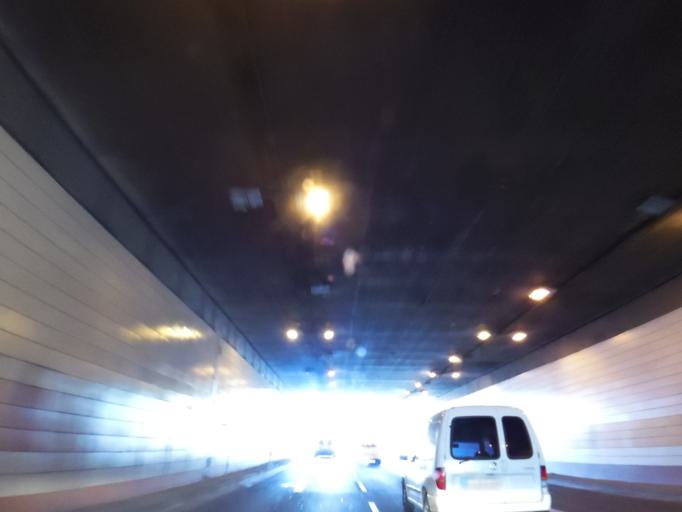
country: DE
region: Thuringia
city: Erfurt
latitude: 50.9734
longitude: 11.0425
